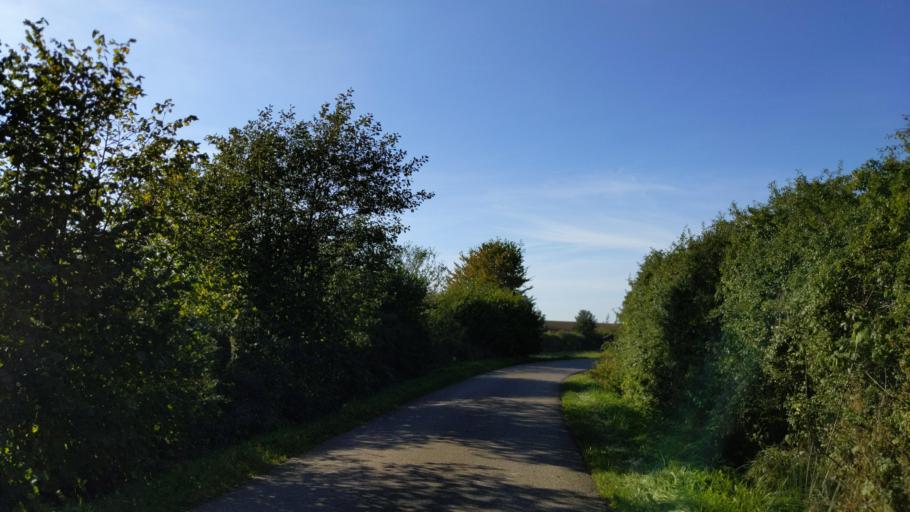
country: DE
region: Schleswig-Holstein
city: Ahrensbok
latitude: 54.0568
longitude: 10.5880
